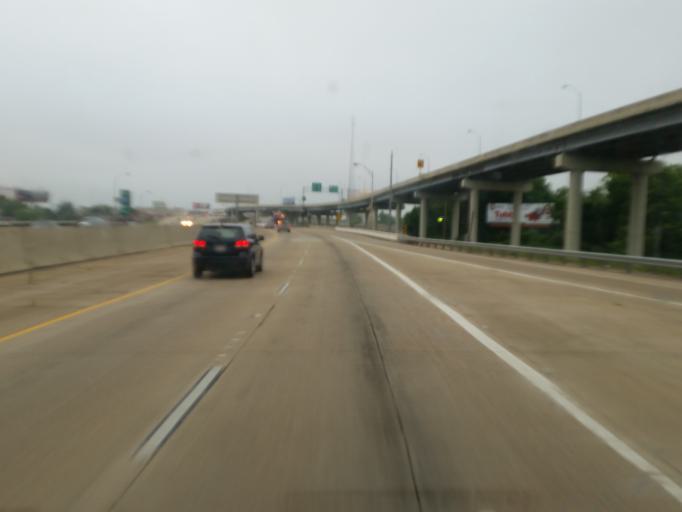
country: US
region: Louisiana
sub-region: Bossier Parish
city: Bossier City
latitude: 32.5039
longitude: -93.7472
